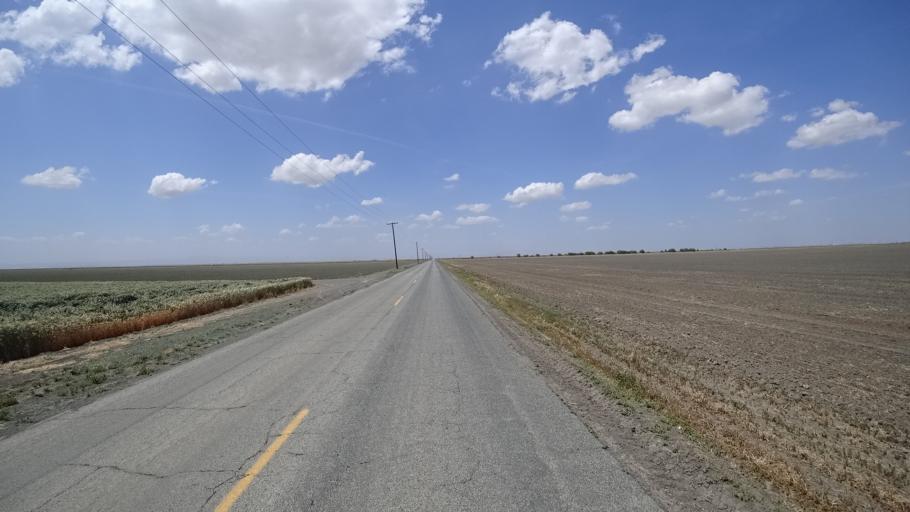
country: US
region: California
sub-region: Kings County
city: Stratford
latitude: 36.1895
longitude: -119.8623
